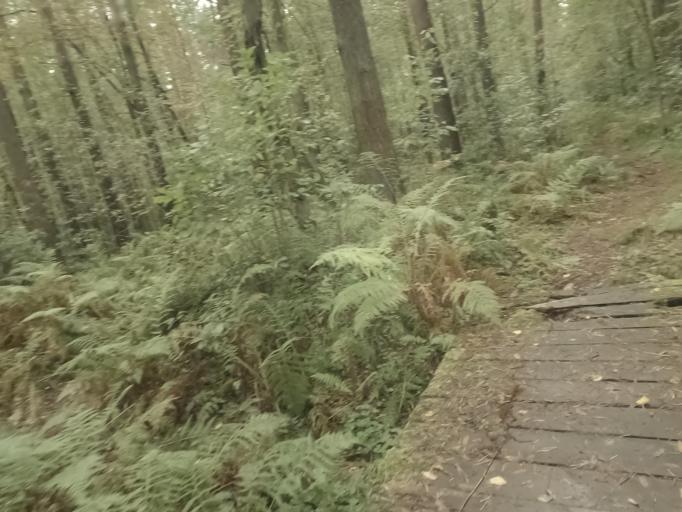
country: RU
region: St.-Petersburg
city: Krasnogvargeisky
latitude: 59.9645
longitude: 30.5074
